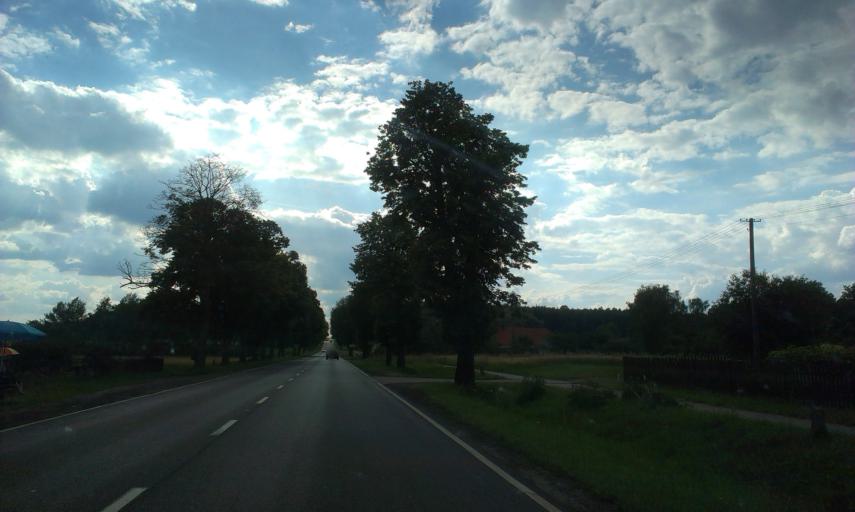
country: PL
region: Greater Poland Voivodeship
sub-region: Powiat pilski
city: Miasteczko Krajenskie
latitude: 53.1326
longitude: 16.9972
